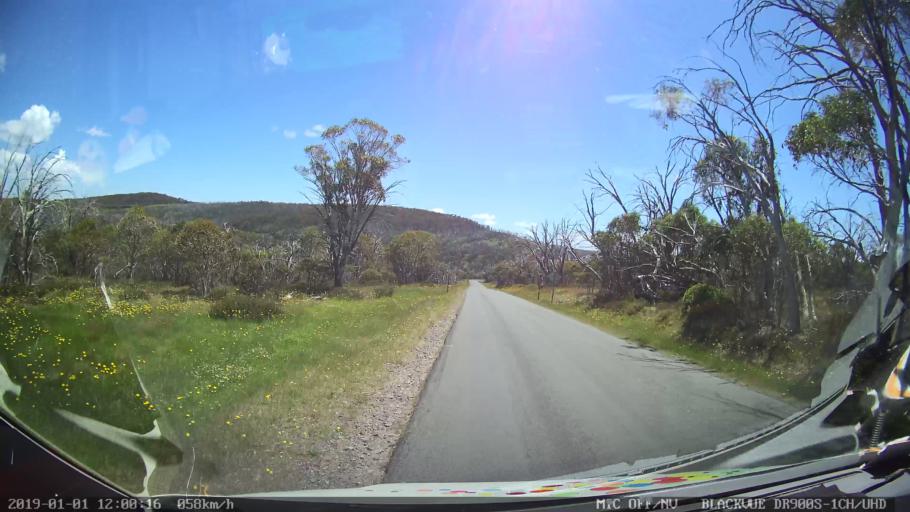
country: AU
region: New South Wales
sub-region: Snowy River
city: Jindabyne
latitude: -35.8863
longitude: 148.4586
